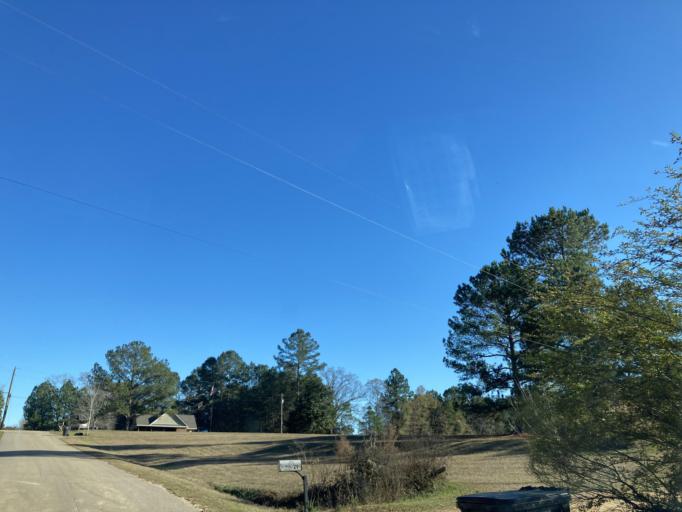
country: US
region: Mississippi
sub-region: Lamar County
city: Sumrall
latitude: 31.3765
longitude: -89.6000
